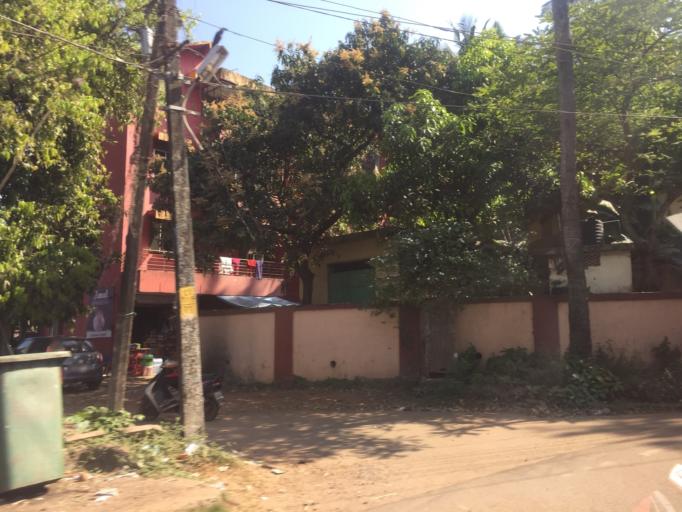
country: IN
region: Goa
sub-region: South Goa
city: Vasco Da Gama
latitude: 15.3966
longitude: 73.8184
